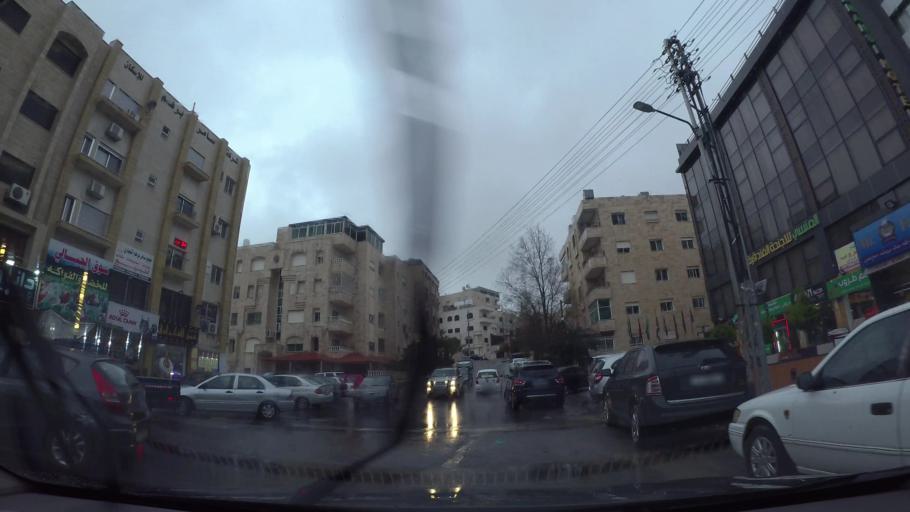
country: JO
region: Amman
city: Al Jubayhah
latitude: 32.0176
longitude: 35.8799
